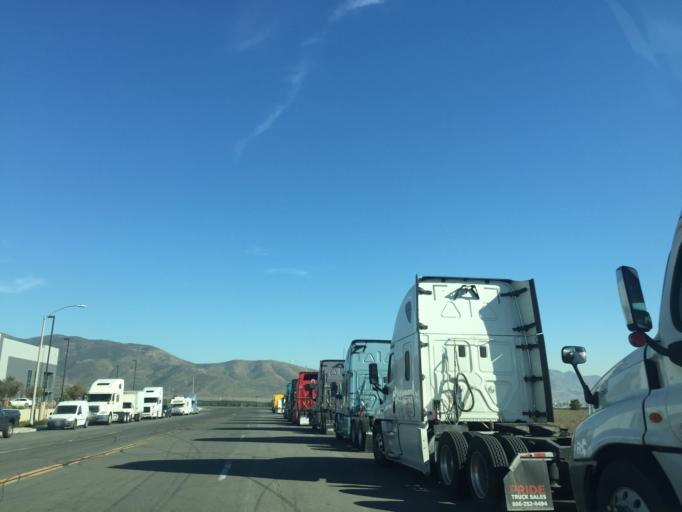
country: MX
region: Baja California
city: Tijuana
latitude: 32.5584
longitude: -116.9254
